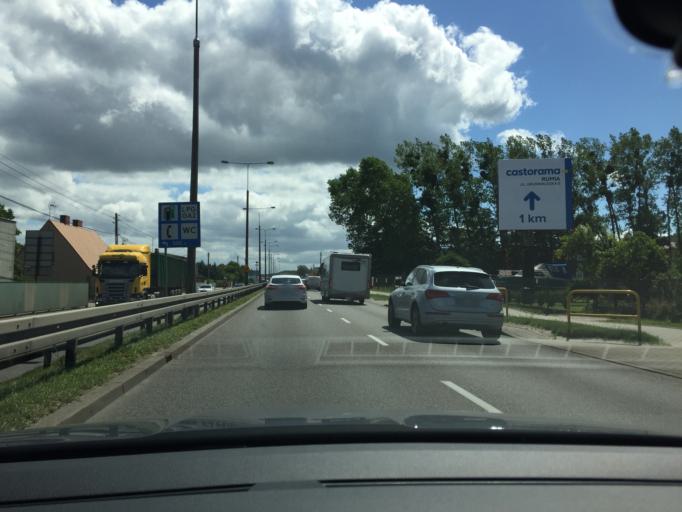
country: PL
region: Pomeranian Voivodeship
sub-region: Powiat wejherowski
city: Rumia
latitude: 54.5795
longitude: 18.3723
